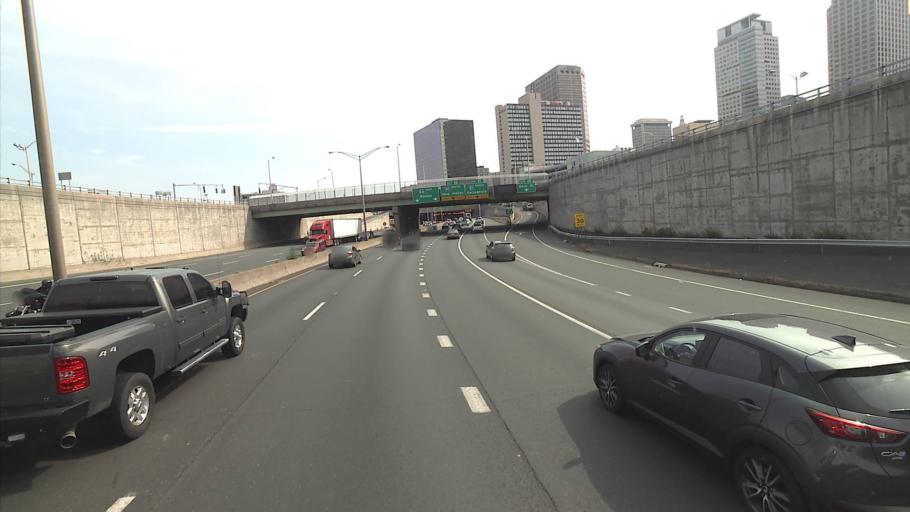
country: US
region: Connecticut
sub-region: Hartford County
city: Hartford
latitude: 41.7709
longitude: -72.6784
